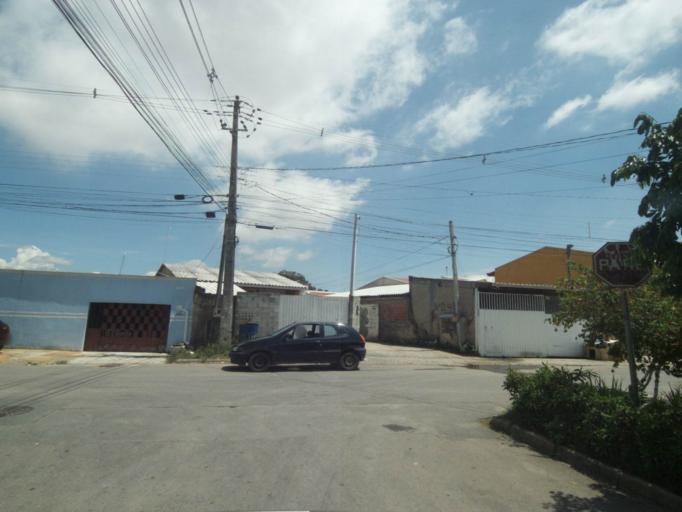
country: BR
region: Parana
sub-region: Pinhais
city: Pinhais
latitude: -25.4730
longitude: -49.1886
